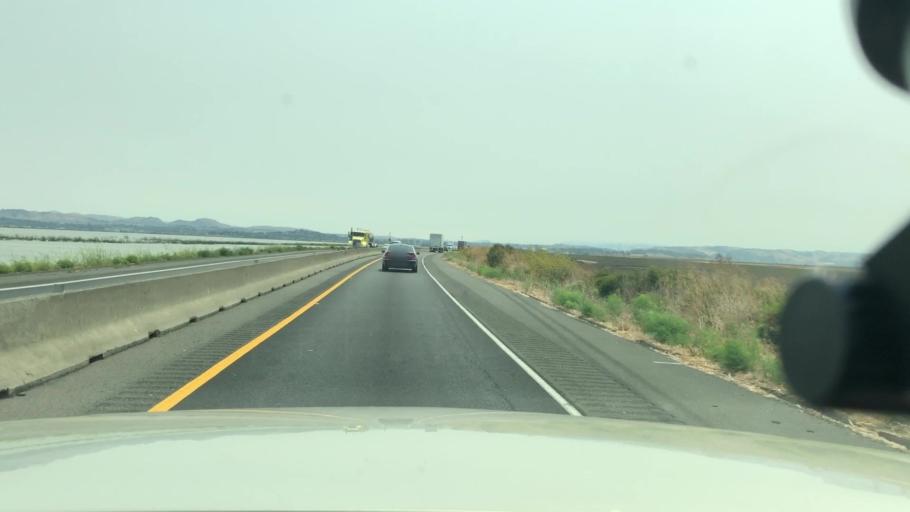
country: US
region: California
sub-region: Solano County
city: Vallejo
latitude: 38.1331
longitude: -122.3400
